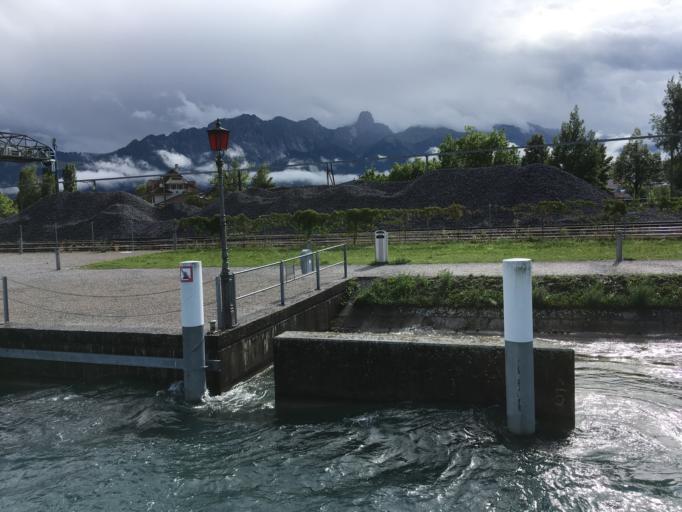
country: CH
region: Bern
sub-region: Thun District
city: Thun
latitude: 46.7502
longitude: 7.6351
